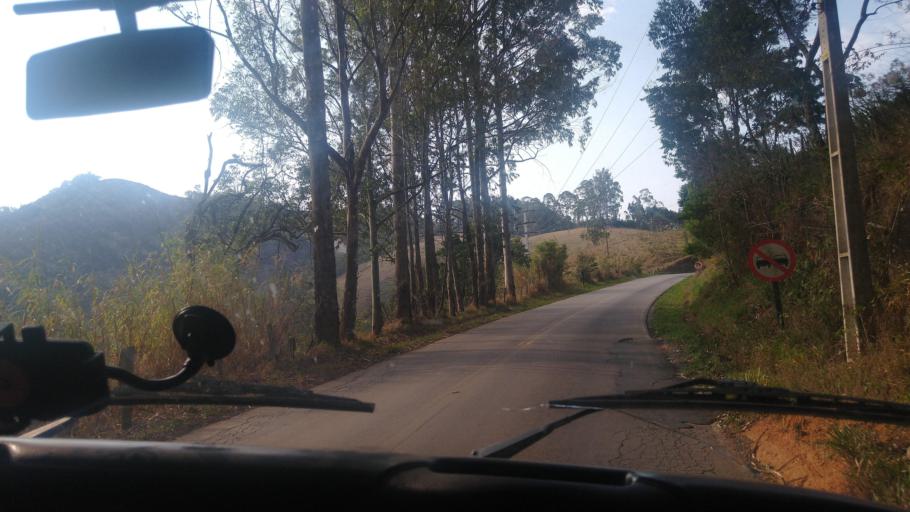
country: BR
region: Minas Gerais
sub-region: Extrema
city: Extrema
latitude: -22.7681
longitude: -46.4374
